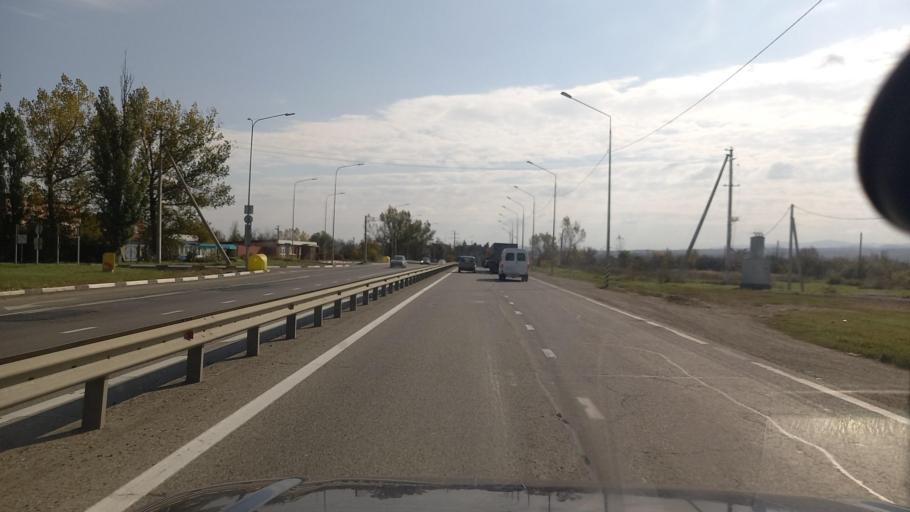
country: RU
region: Krasnodarskiy
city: Akhtyrskiy
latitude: 44.8482
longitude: 38.2772
